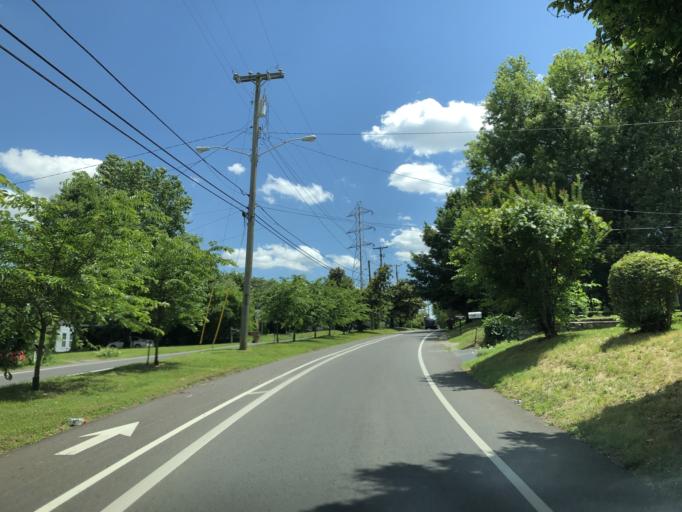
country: US
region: Tennessee
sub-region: Davidson County
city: Nashville
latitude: 36.1842
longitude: -86.7253
